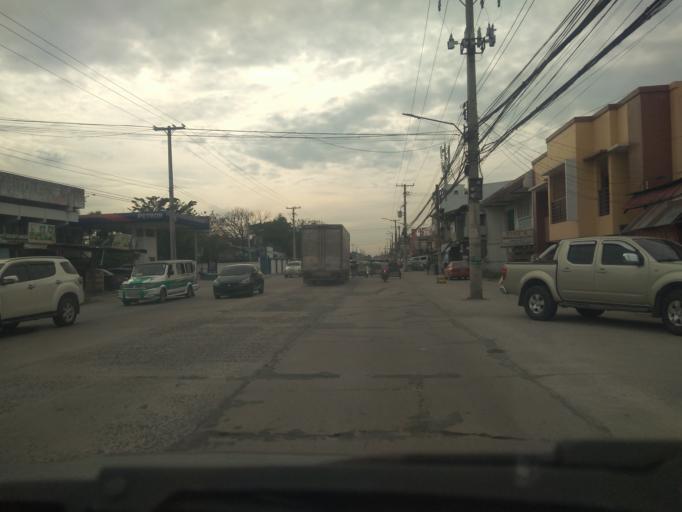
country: PH
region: Central Luzon
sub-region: Province of Pampanga
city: San Fernando
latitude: 15.0189
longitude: 120.7009
